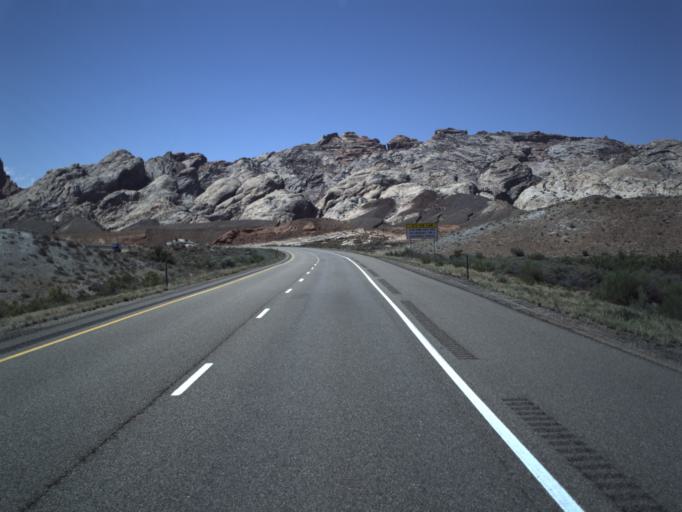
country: US
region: Utah
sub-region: Carbon County
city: East Carbon City
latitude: 38.9245
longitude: -110.4080
